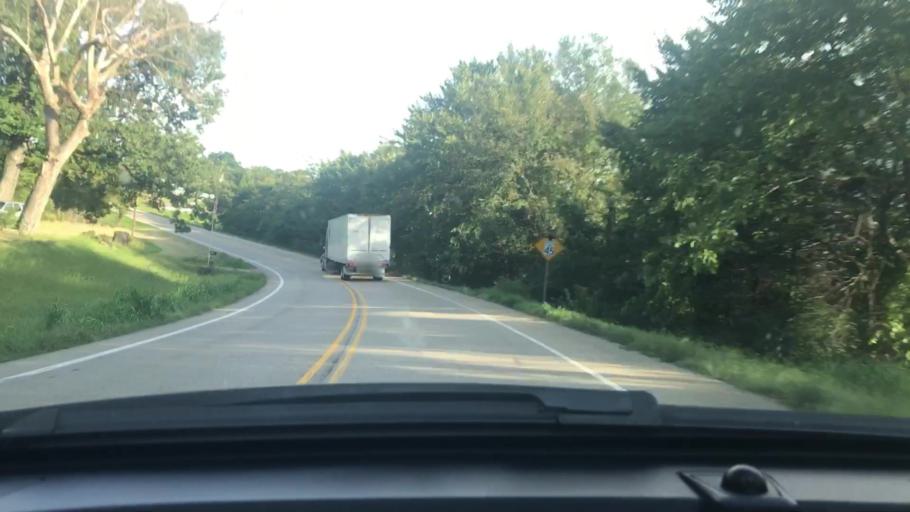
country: US
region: Arkansas
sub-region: Sharp County
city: Cherokee Village
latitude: 36.2406
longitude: -91.2649
